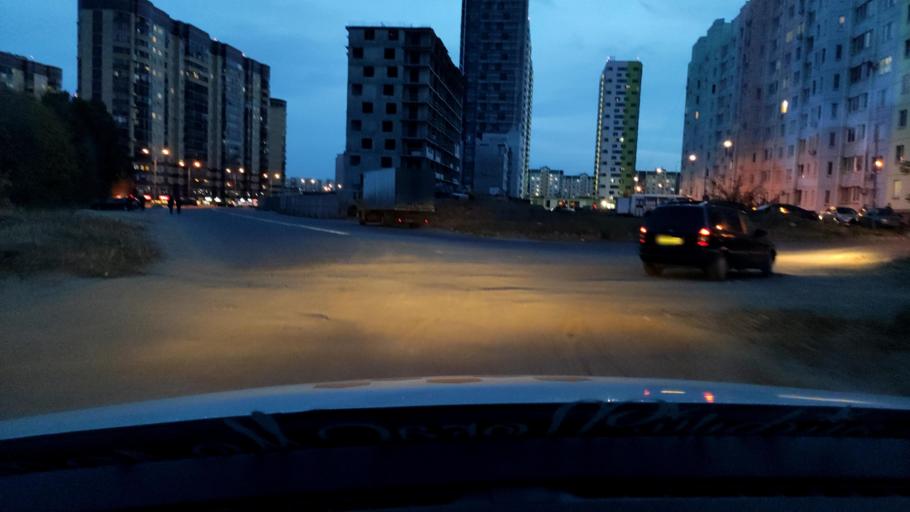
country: RU
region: Voronezj
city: Podgornoye
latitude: 51.7176
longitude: 39.1908
